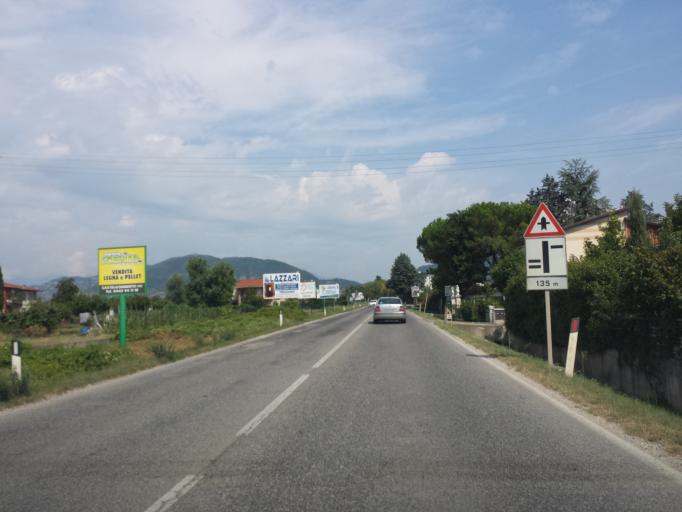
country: IT
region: Veneto
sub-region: Provincia di Vicenza
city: Castelgomberto
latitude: 45.5756
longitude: 11.3834
